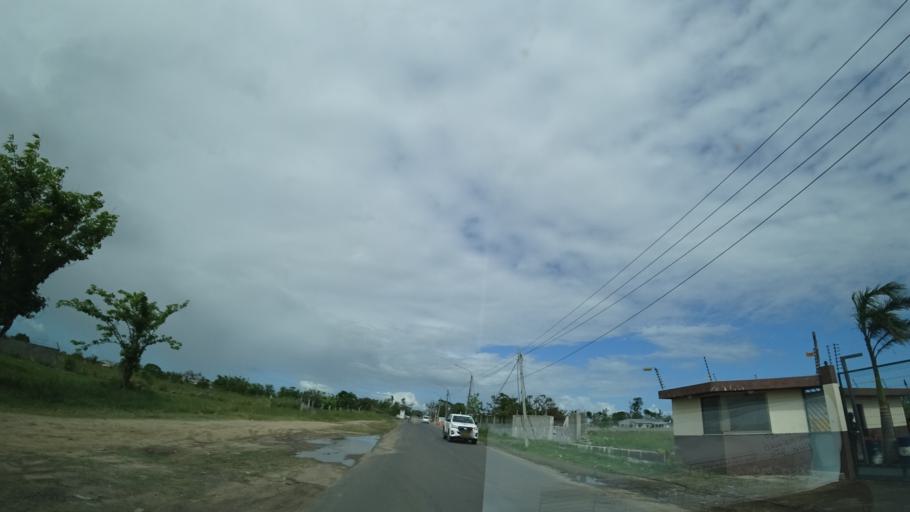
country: MZ
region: Sofala
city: Beira
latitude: -19.8025
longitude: 34.9018
